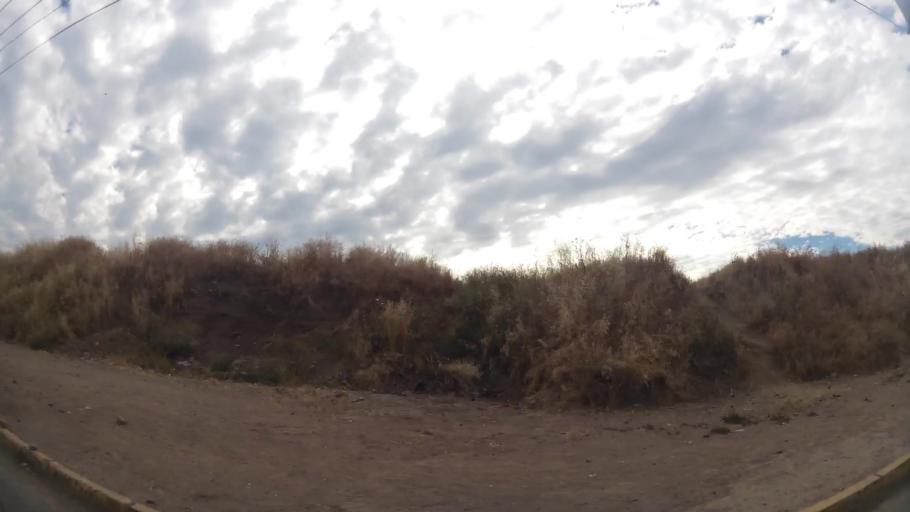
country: CL
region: Santiago Metropolitan
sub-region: Provincia de Santiago
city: La Pintana
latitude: -33.6233
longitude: -70.6178
